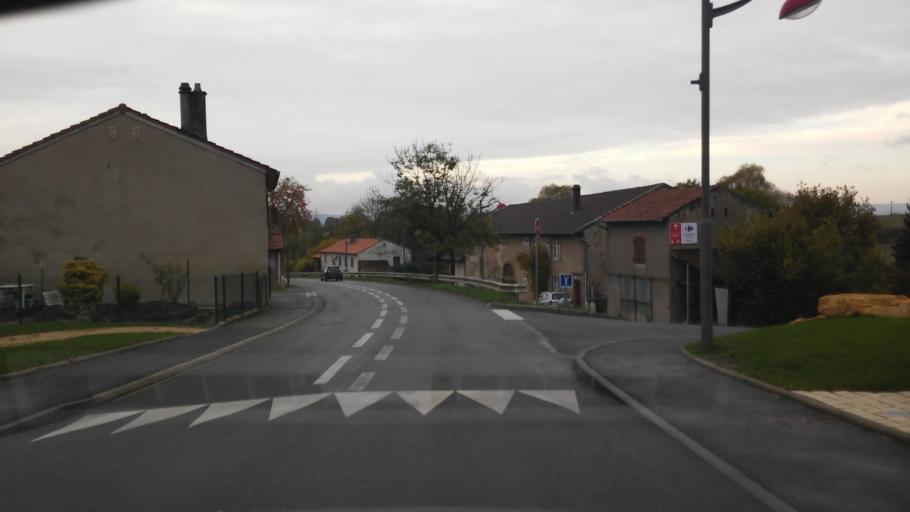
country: FR
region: Lorraine
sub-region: Departement de la Moselle
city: Ennery
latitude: 49.1952
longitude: 6.2480
